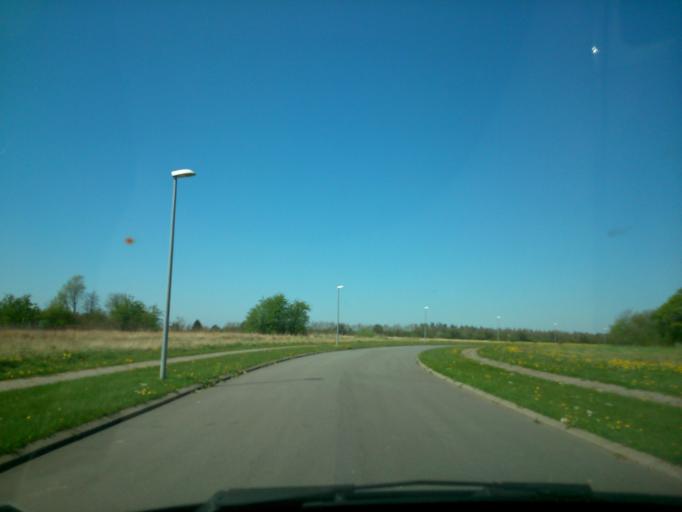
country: DK
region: South Denmark
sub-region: Varde Kommune
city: Olgod
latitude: 55.8118
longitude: 8.6073
